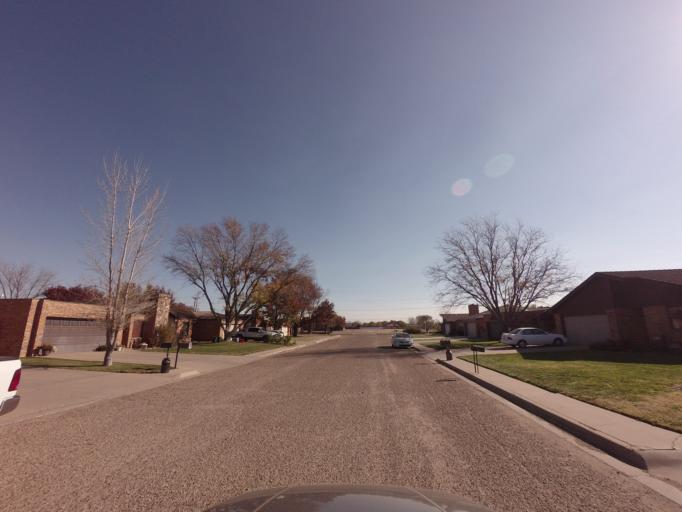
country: US
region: New Mexico
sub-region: Curry County
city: Clovis
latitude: 34.4137
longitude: -103.1798
